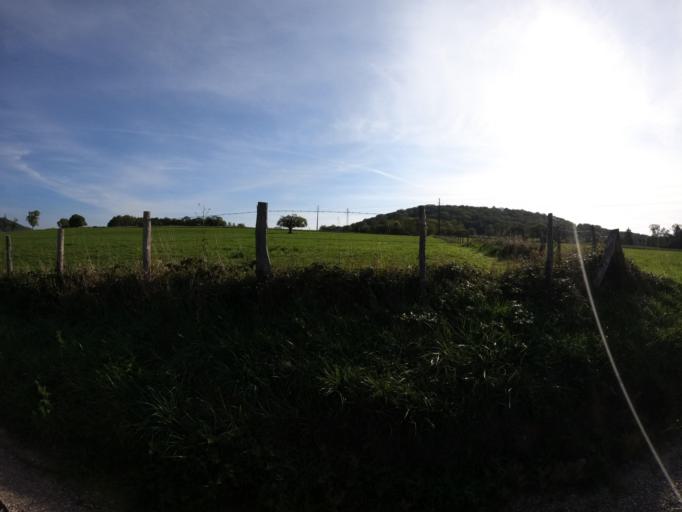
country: FR
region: Franche-Comte
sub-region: Departement du Jura
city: Montmorot
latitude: 46.6897
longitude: 5.5355
